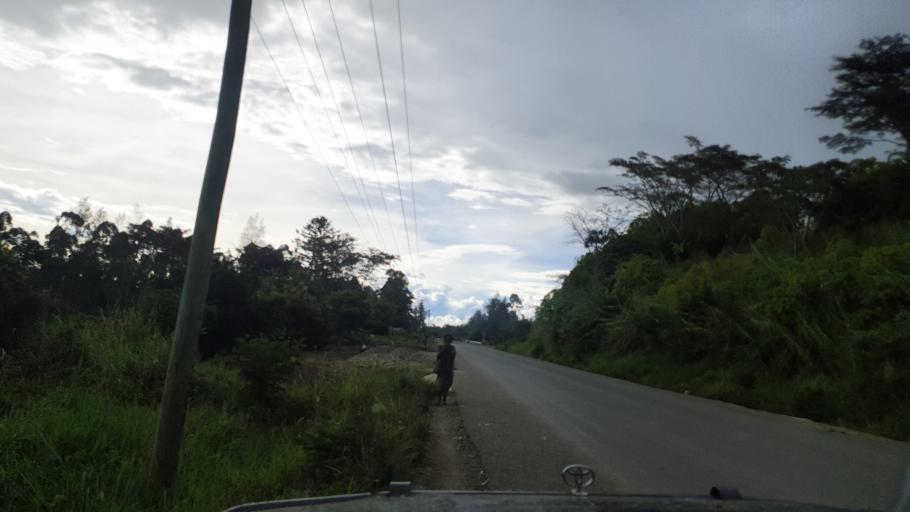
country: PG
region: Jiwaka
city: Minj
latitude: -5.9376
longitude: 144.8070
